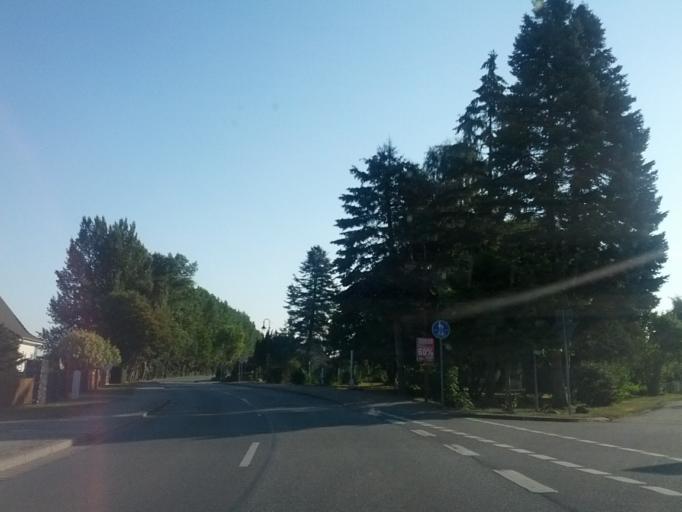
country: DE
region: Mecklenburg-Vorpommern
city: Brandshagen
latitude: 54.1944
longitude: 13.1875
